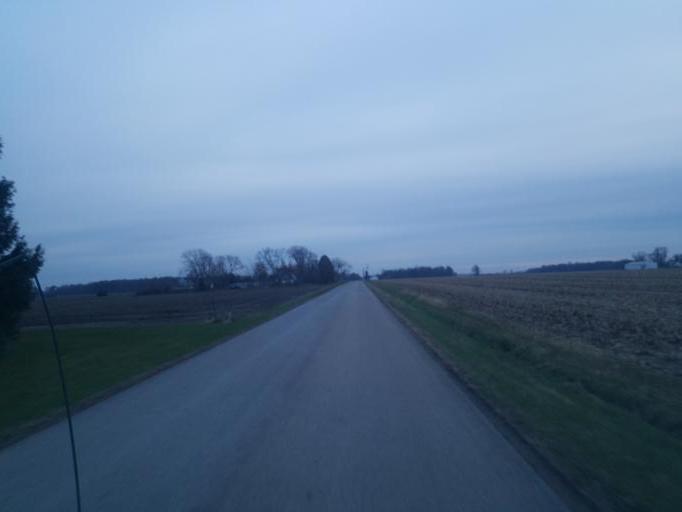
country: US
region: Indiana
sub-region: Adams County
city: Decatur
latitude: 40.7773
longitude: -85.0145
